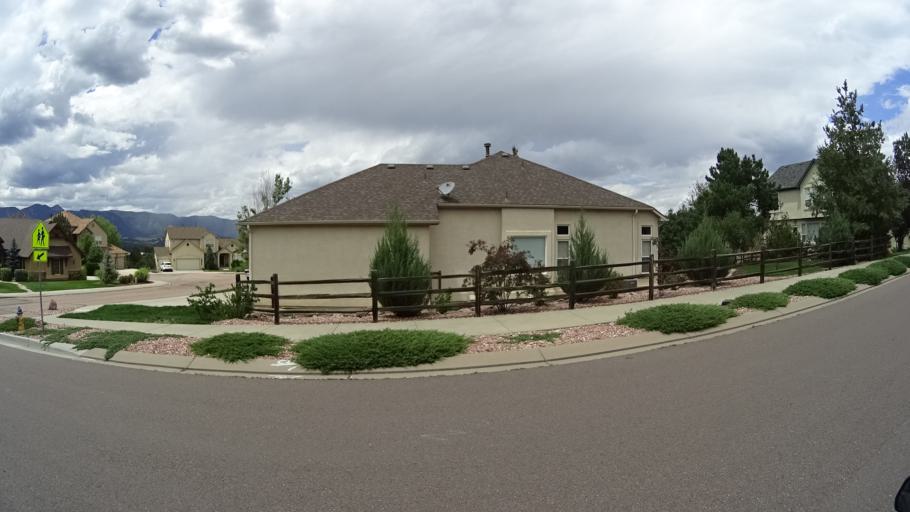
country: US
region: Colorado
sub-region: El Paso County
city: Gleneagle
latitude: 39.0164
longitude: -104.8069
